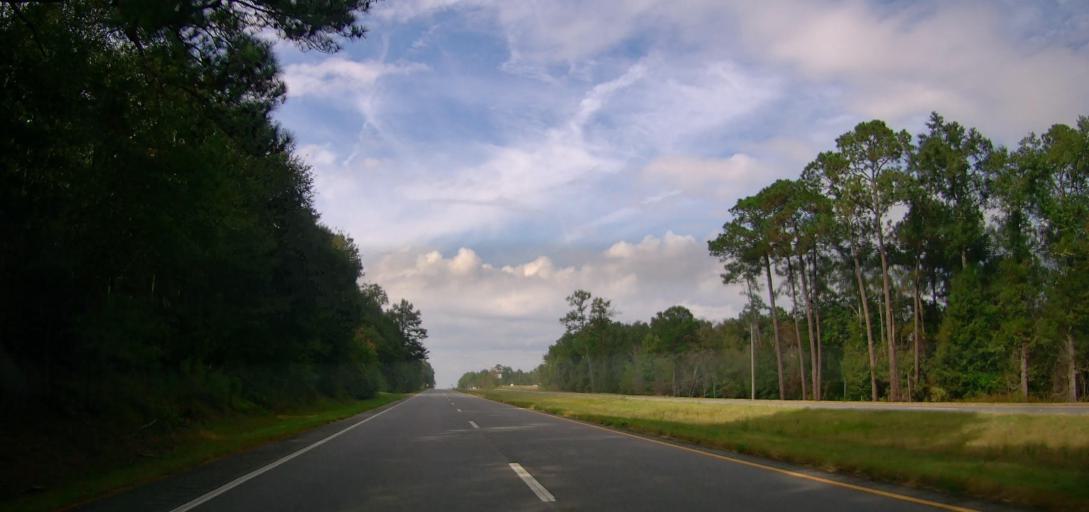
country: US
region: Georgia
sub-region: Thomas County
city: Meigs
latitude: 30.9713
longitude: -84.0344
